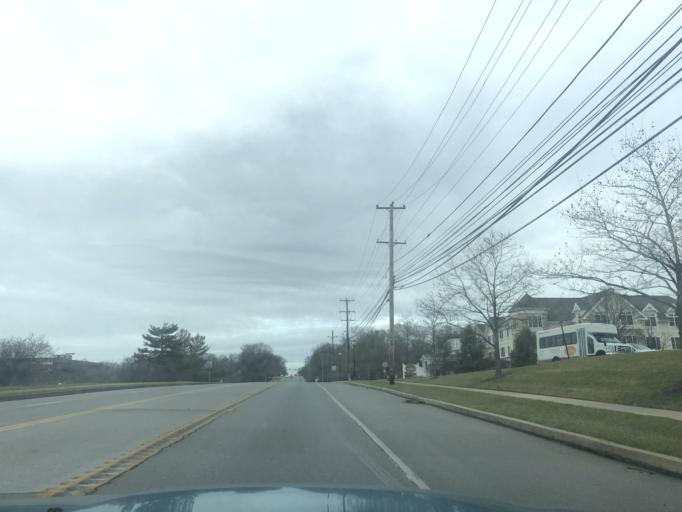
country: US
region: Pennsylvania
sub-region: Montgomery County
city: Dresher
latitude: 40.1434
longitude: -75.1709
